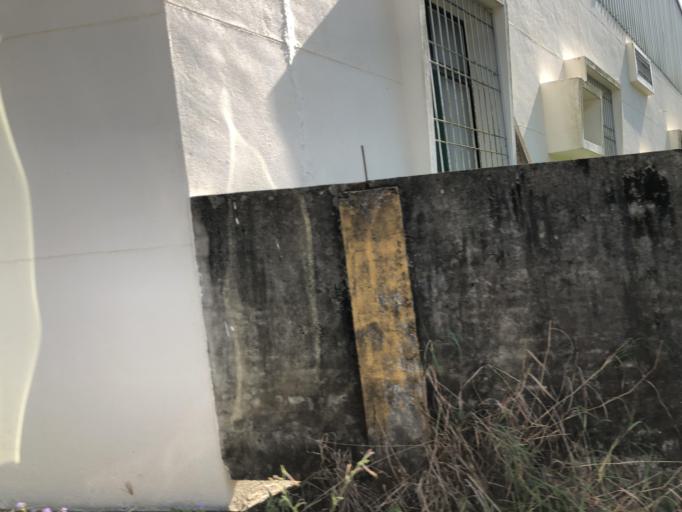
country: TW
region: Taiwan
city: Yujing
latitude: 23.0451
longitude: 120.3653
